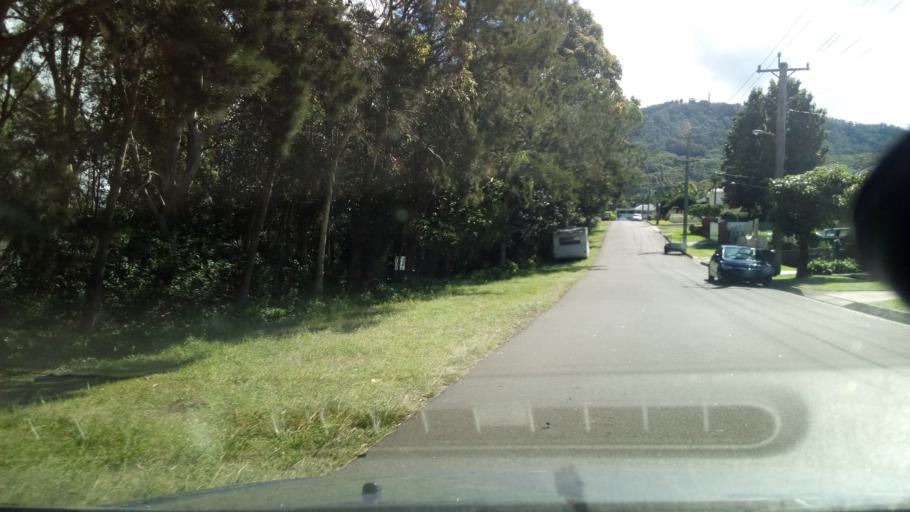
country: AU
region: New South Wales
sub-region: Wollongong
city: Mount Ousley
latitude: -34.4008
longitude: 150.8784
